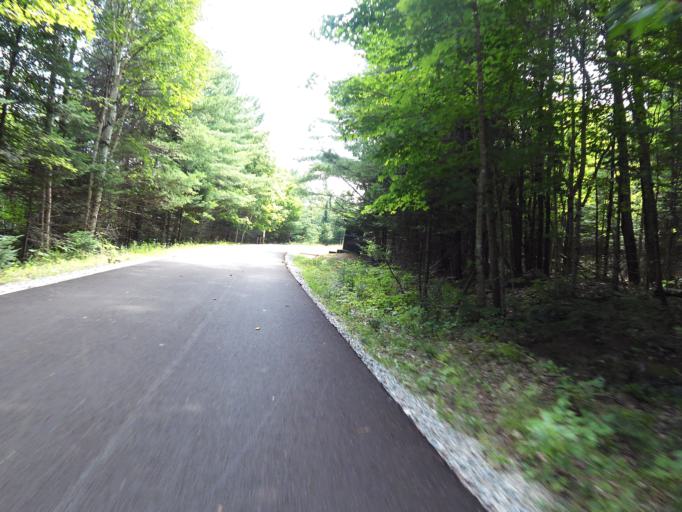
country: CA
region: Quebec
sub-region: Outaouais
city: Maniwaki
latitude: 46.1404
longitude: -76.0336
